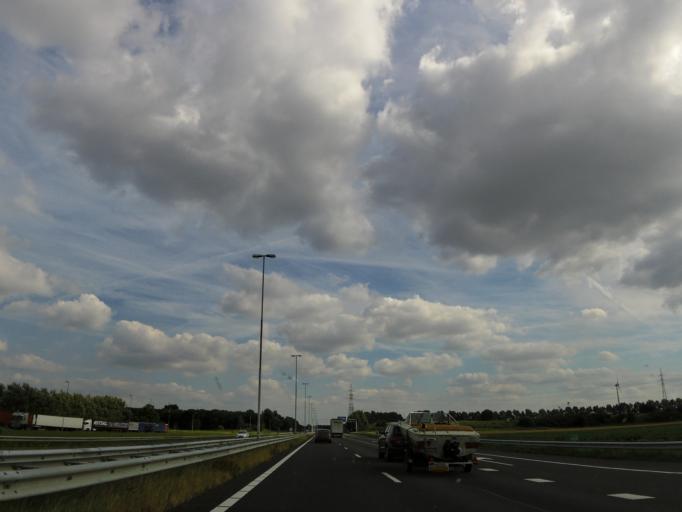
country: NL
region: North Brabant
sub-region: Gemeente Woensdrecht
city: Woensdrecht
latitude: 51.3800
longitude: 4.3022
